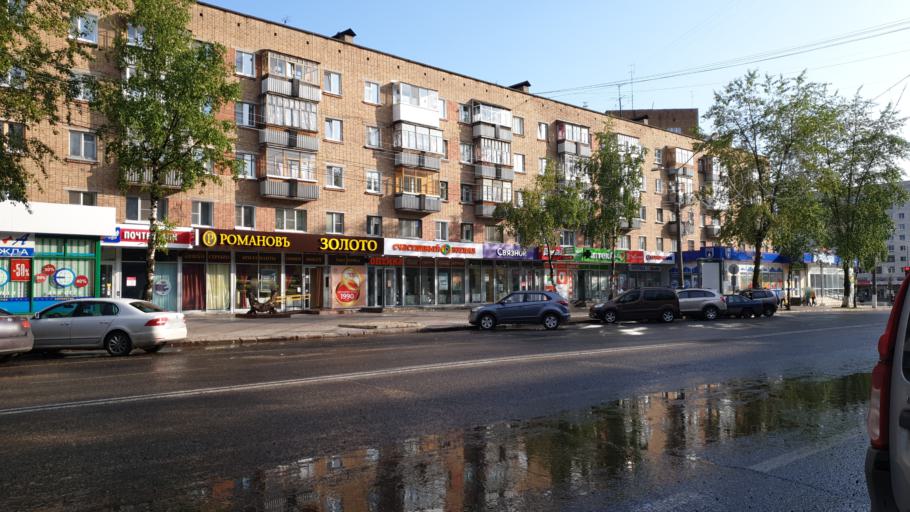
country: RU
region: Komi Republic
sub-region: Syktyvdinskiy Rayon
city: Syktyvkar
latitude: 61.6645
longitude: 50.8187
